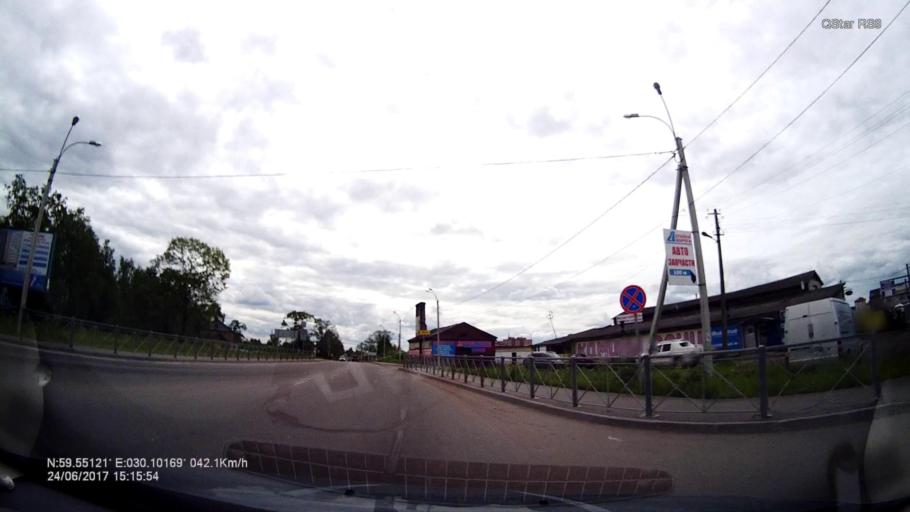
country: RU
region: Leningrad
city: Gatchina
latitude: 59.5512
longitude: 30.1016
